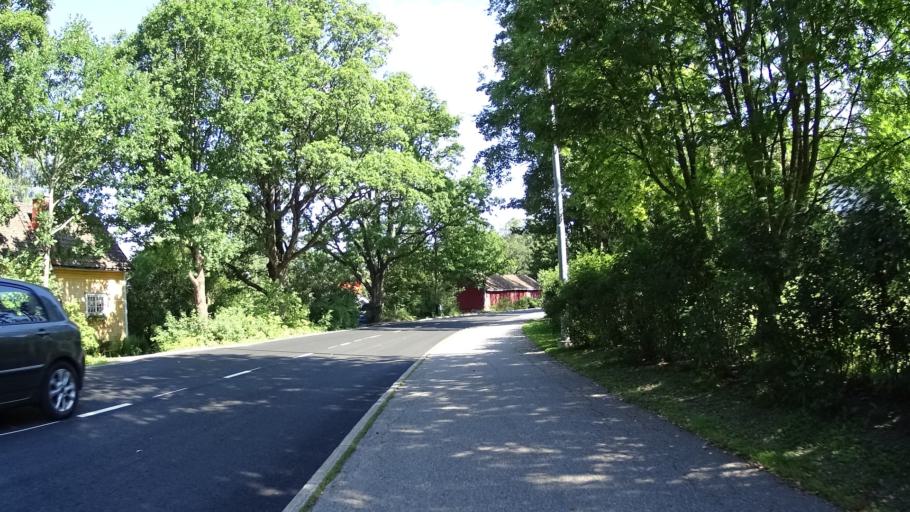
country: FI
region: Uusimaa
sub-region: Helsinki
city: Tuusula
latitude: 60.4101
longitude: 25.0300
